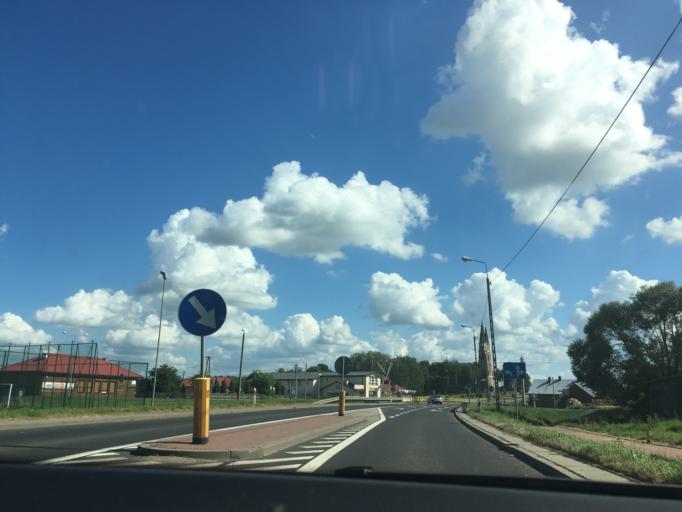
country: PL
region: Podlasie
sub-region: Powiat sokolski
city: Suchowola
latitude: 53.4451
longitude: 23.0939
